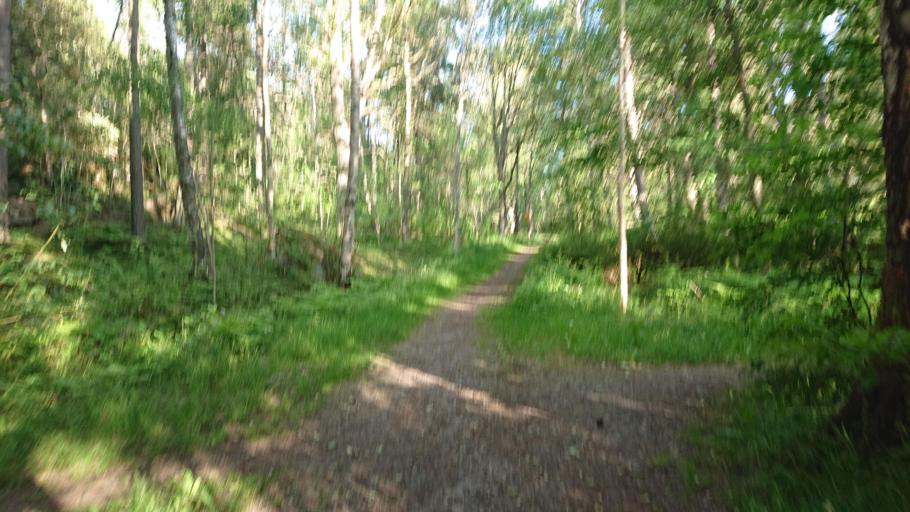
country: SE
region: Stockholm
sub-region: Osterakers Kommun
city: Akersberga
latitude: 59.4919
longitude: 18.3032
